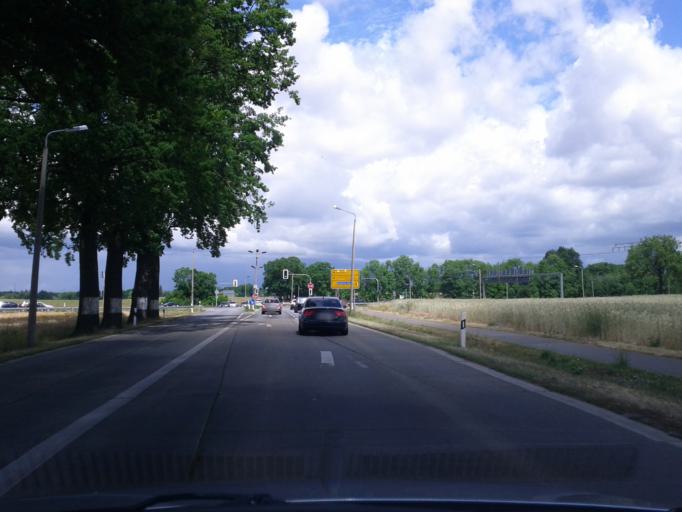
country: DE
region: Brandenburg
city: Schoneiche
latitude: 52.4998
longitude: 13.7013
